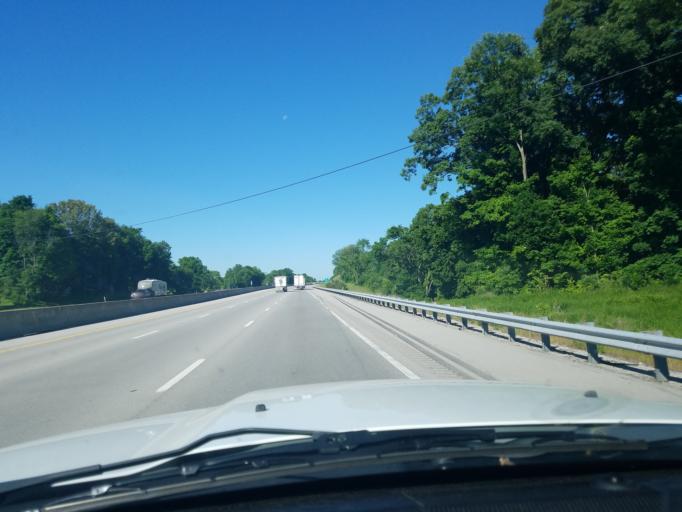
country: US
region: Kentucky
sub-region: Barren County
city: Cave City
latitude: 37.0684
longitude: -86.0936
